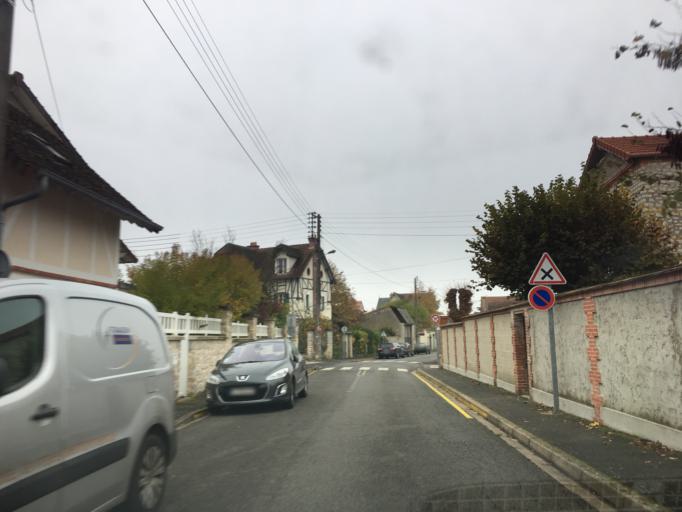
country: FR
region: Ile-de-France
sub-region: Departement de Seine-et-Marne
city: Moret-sur-Loing
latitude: 48.3720
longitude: 2.8127
